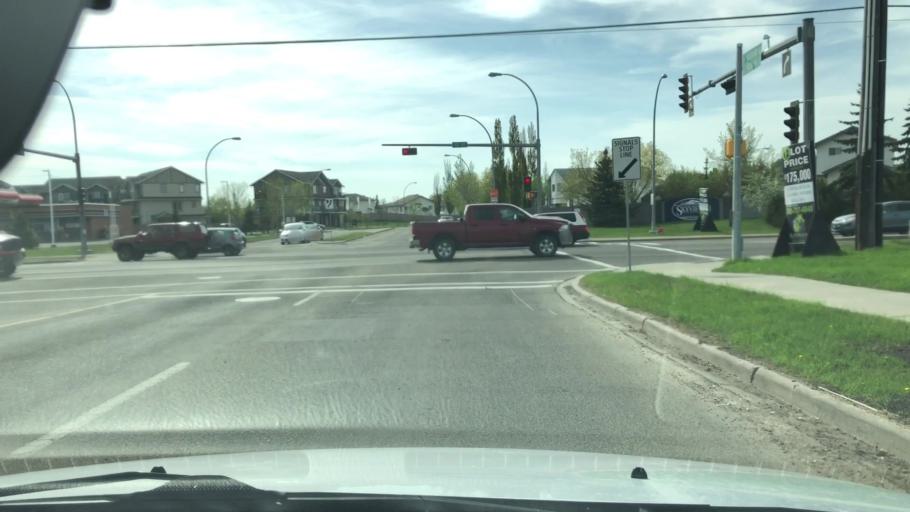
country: CA
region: Alberta
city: Edmonton
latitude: 53.6042
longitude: -113.5408
